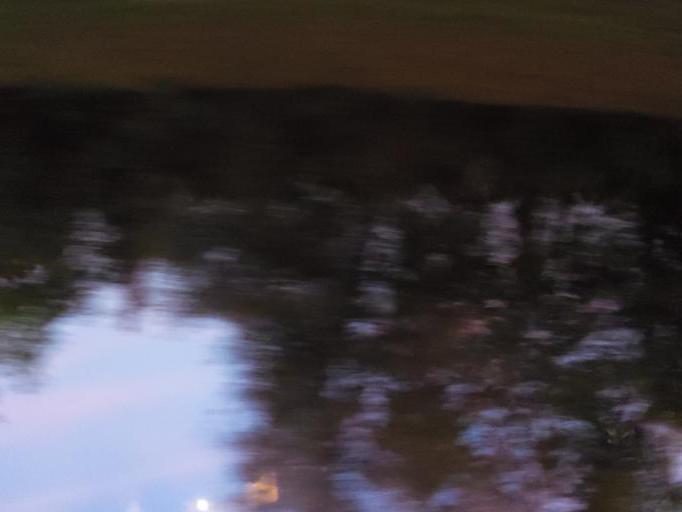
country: US
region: Florida
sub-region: Volusia County
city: De Leon Springs
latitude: 29.1726
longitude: -81.3018
